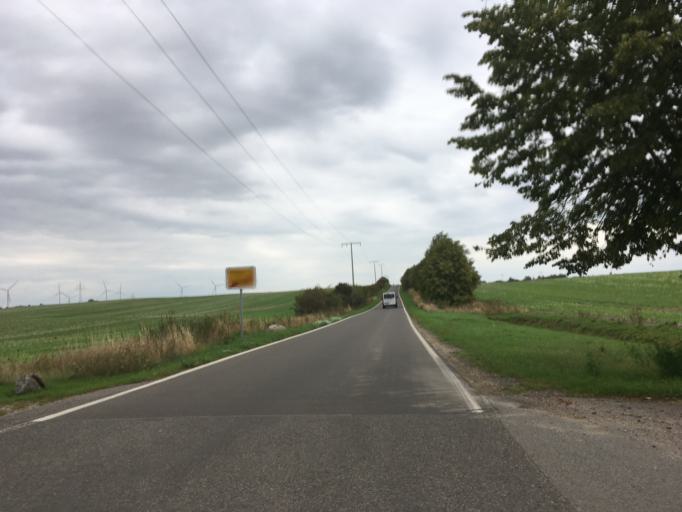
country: DE
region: Brandenburg
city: Pinnow
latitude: 53.0552
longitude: 14.0575
